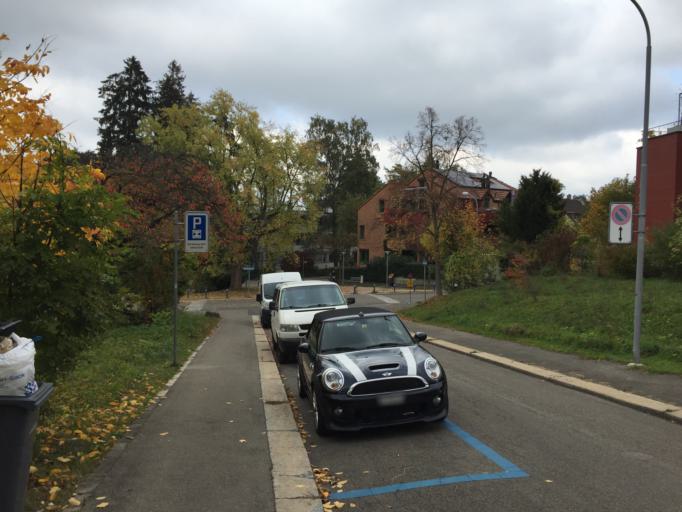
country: CH
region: Zurich
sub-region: Bezirk Zuerich
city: Zuerich (Kreis 11) / Oerlikon
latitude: 47.4046
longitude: 8.5423
